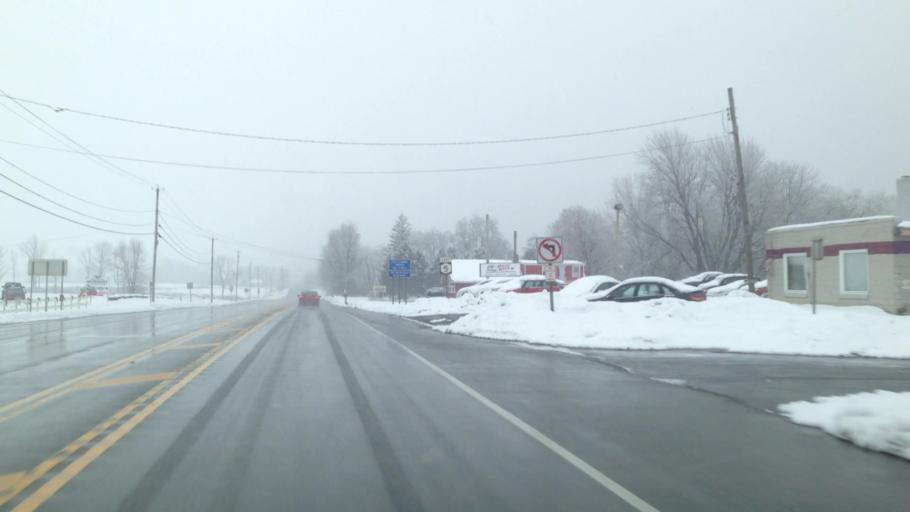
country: US
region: New York
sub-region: Onondaga County
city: Marcellus
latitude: 43.0346
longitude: -76.3648
